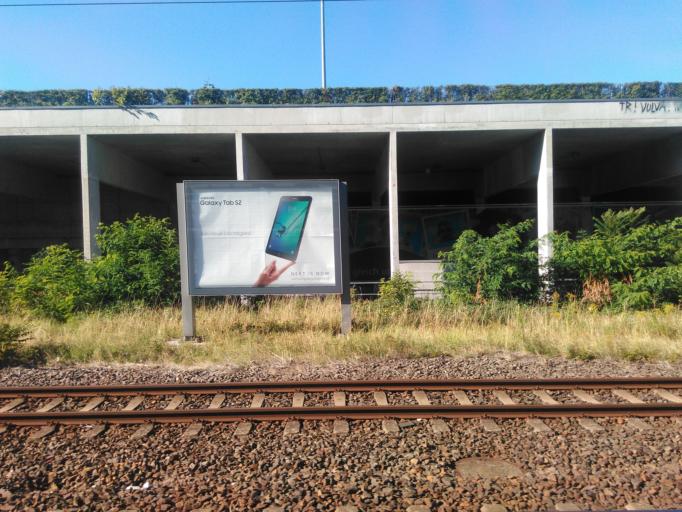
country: DE
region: Berlin
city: Friedrichshain Bezirk
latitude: 52.5294
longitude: 13.4545
